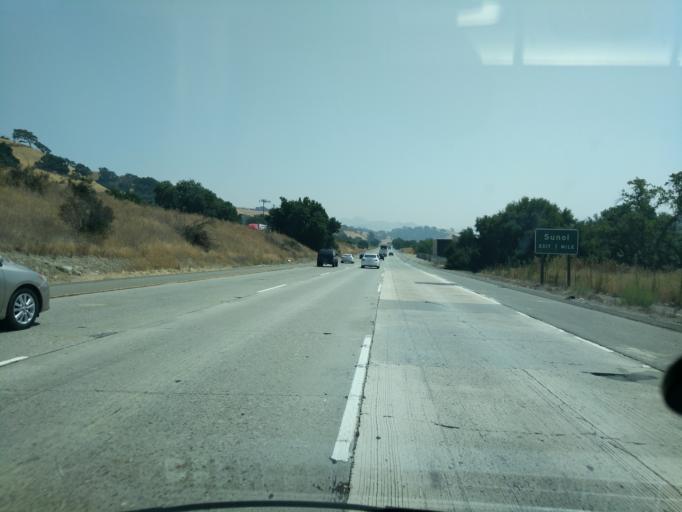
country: US
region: California
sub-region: Alameda County
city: Pleasanton
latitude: 37.6188
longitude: -121.8786
